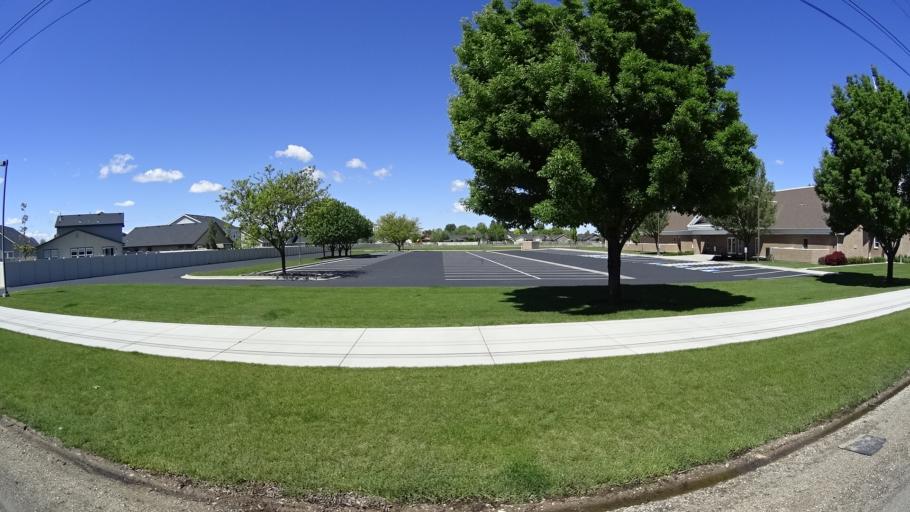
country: US
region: Idaho
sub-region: Ada County
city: Meridian
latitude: 43.6545
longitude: -116.3746
